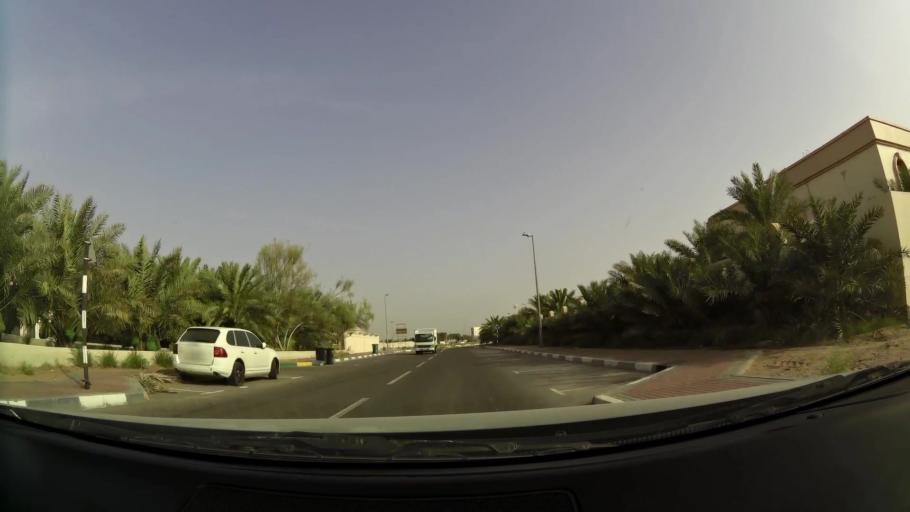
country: AE
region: Abu Dhabi
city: Al Ain
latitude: 24.1315
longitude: 55.6882
